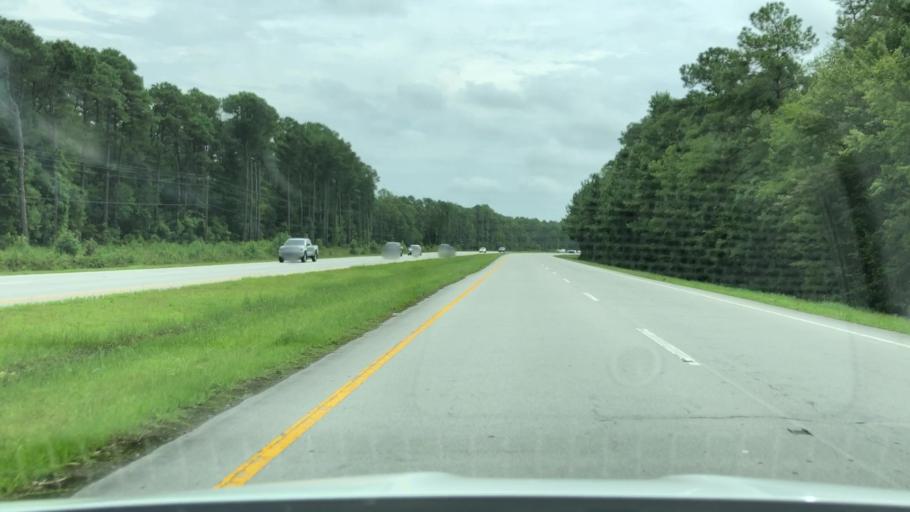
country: US
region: North Carolina
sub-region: Craven County
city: Havelock
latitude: 34.8524
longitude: -76.8906
